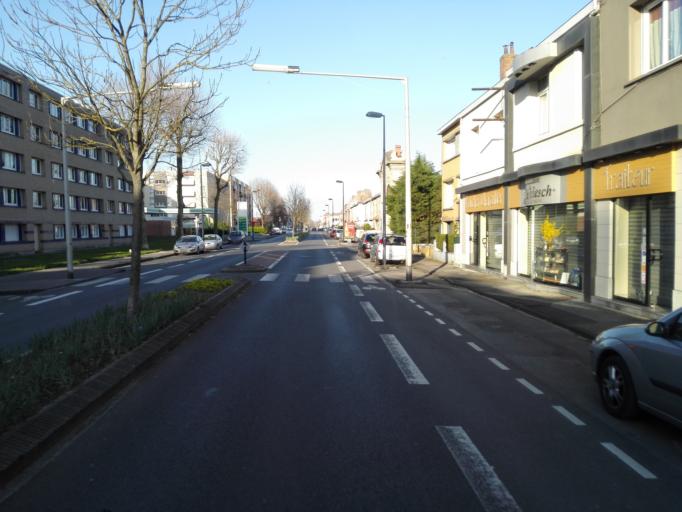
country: FR
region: Nord-Pas-de-Calais
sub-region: Departement du Nord
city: Coudekerque-Branche
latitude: 51.0472
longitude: 2.4137
